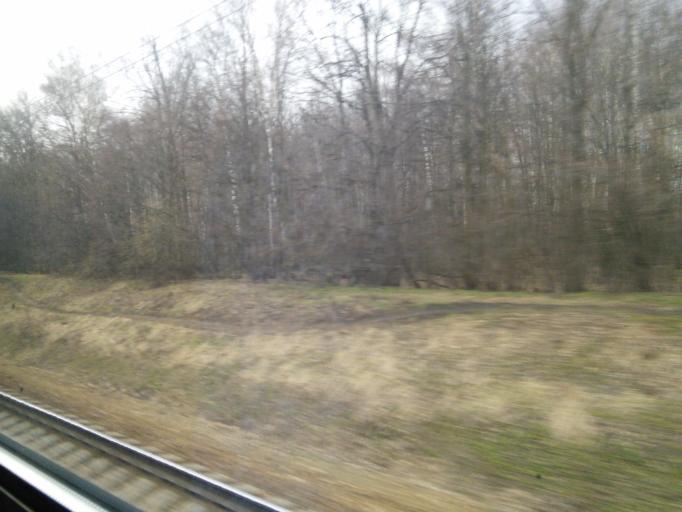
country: RU
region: Moskovskaya
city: Klimovsk
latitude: 55.3890
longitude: 37.5373
